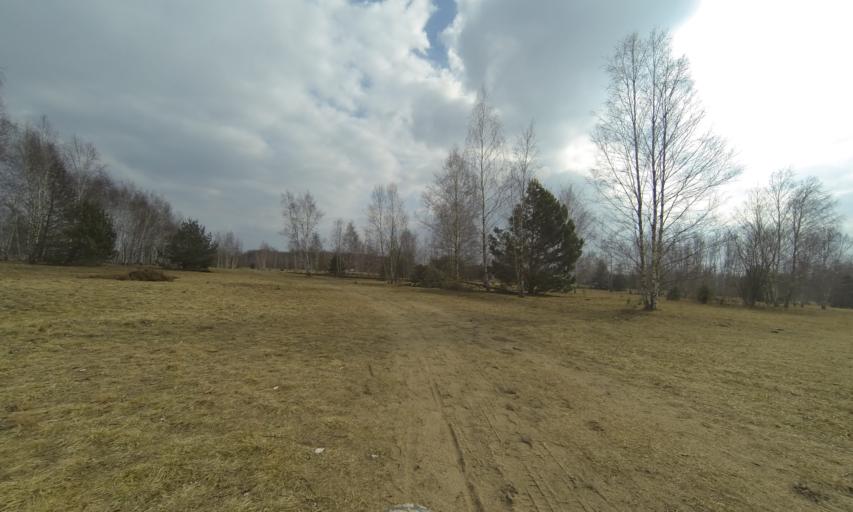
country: DE
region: Saxony
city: Albertstadt
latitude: 51.0975
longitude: 13.7437
